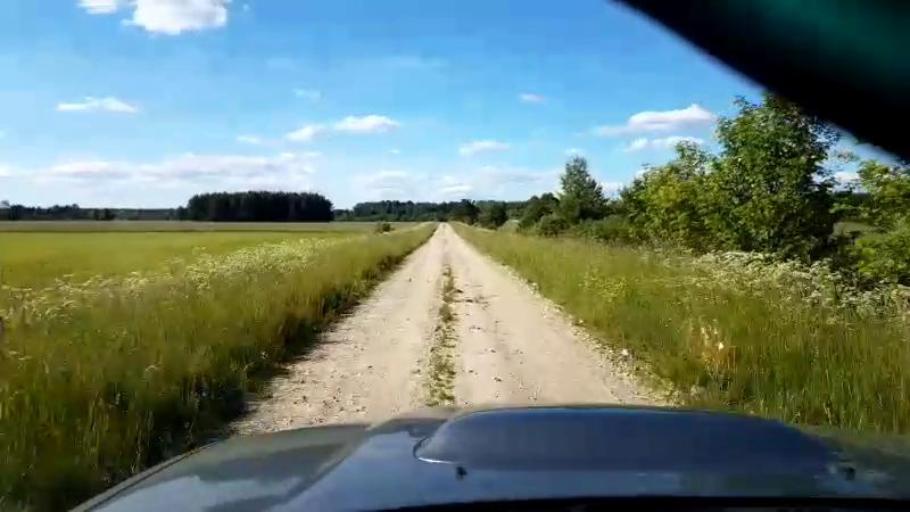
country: EE
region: Paernumaa
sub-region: Sauga vald
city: Sauga
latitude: 58.5063
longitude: 24.5903
